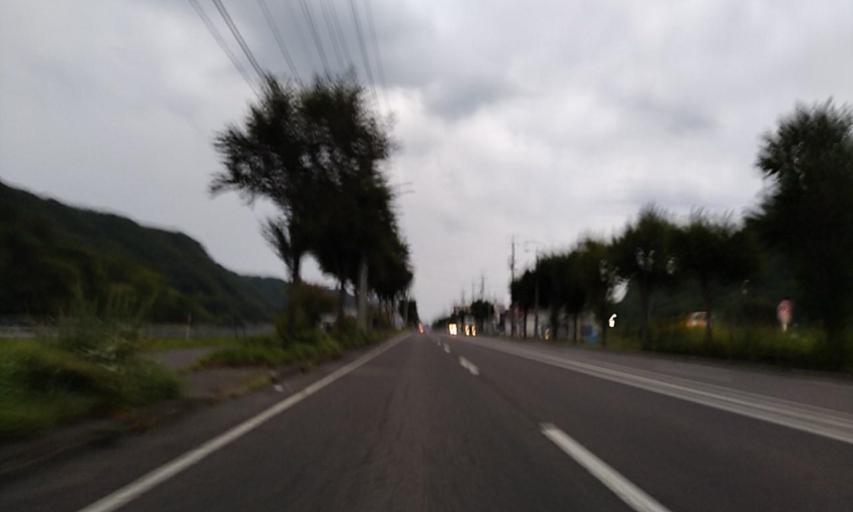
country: JP
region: Hokkaido
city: Abashiri
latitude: 44.0150
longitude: 144.2399
